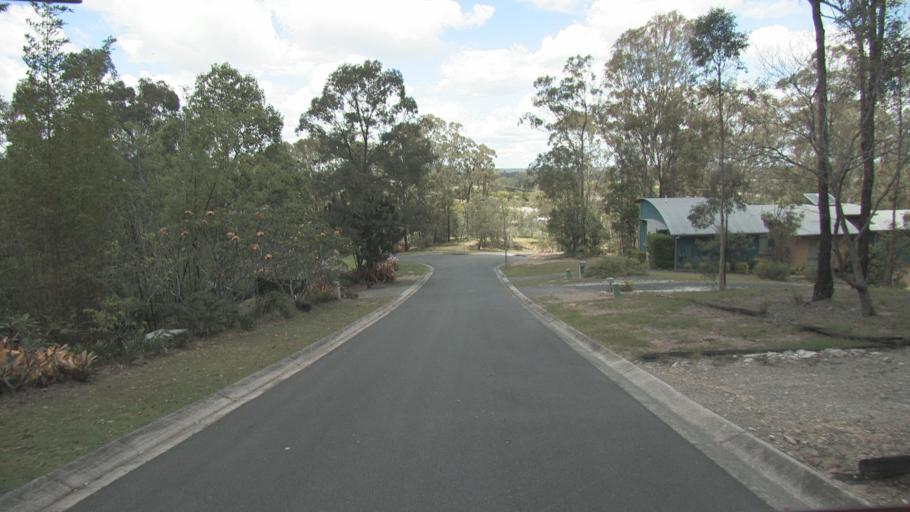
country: AU
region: Queensland
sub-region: Logan
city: Beenleigh
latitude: -27.6737
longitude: 153.2213
